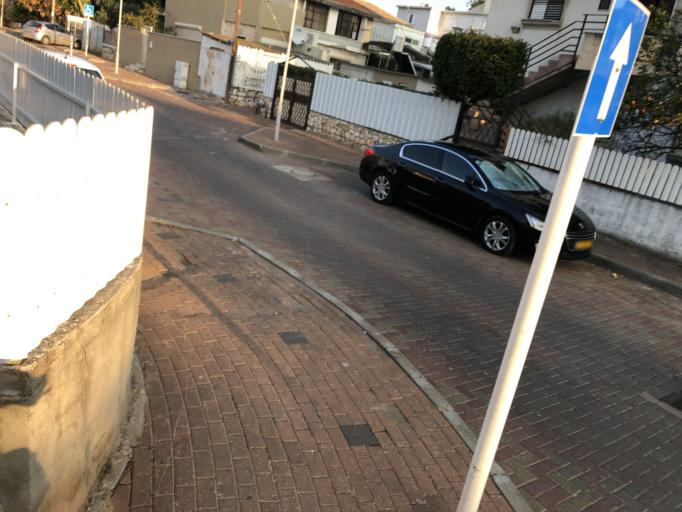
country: IL
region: Northern District
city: `Akko
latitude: 32.9268
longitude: 35.0849
